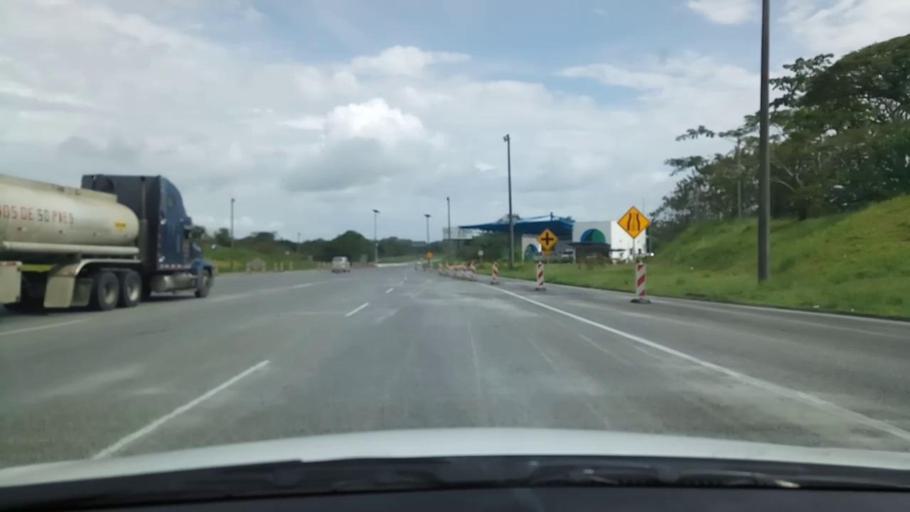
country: PA
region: Colon
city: Buena Vista
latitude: 9.2626
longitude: -79.7001
